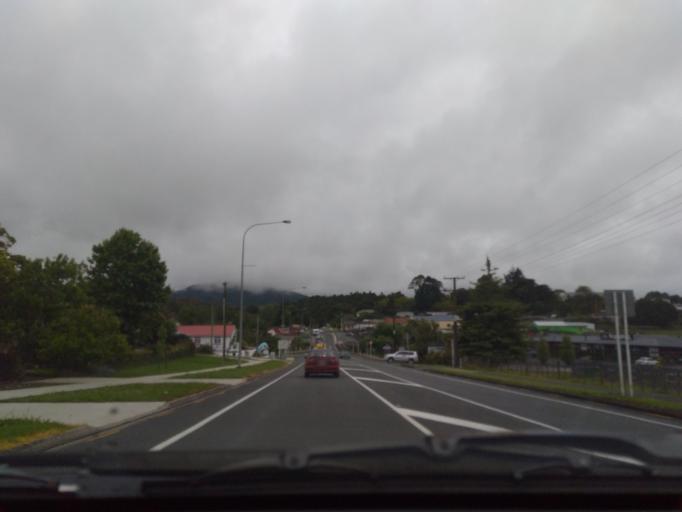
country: NZ
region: Auckland
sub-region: Auckland
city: Wellsford
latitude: -36.1637
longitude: 174.4432
